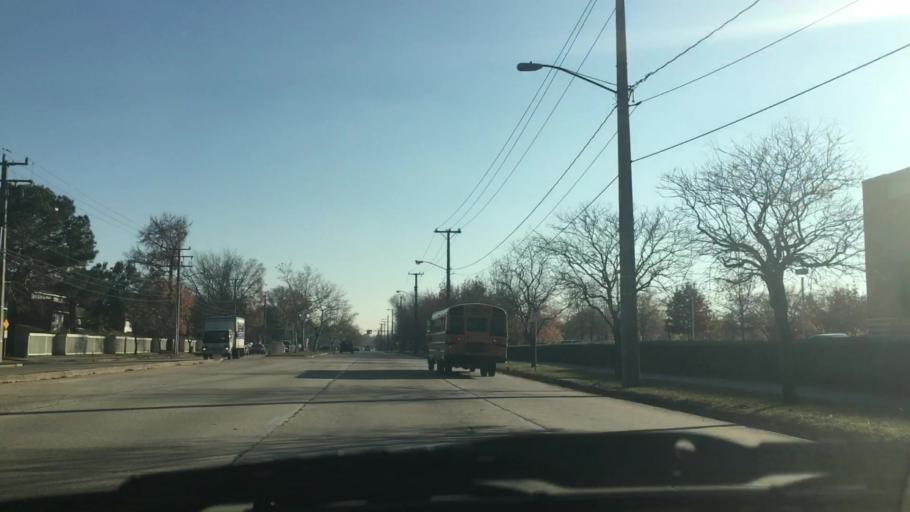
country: US
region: Virginia
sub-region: City of Norfolk
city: Norfolk
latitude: 36.9003
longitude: -76.2393
